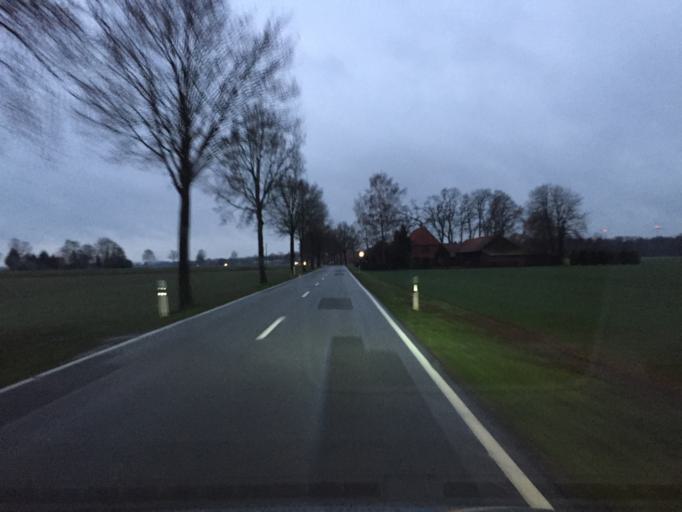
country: DE
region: Lower Saxony
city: Sudwalde
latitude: 52.7747
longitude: 8.8333
